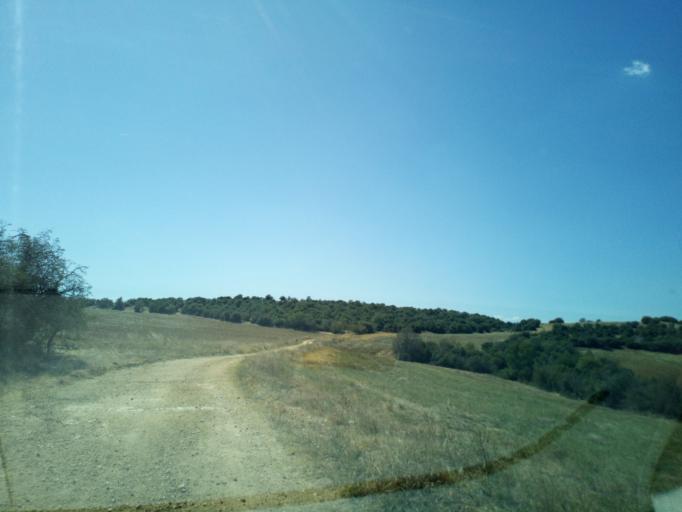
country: GR
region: Central Macedonia
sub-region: Nomos Thessalonikis
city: Gerakarou
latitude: 40.7282
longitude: 23.2382
